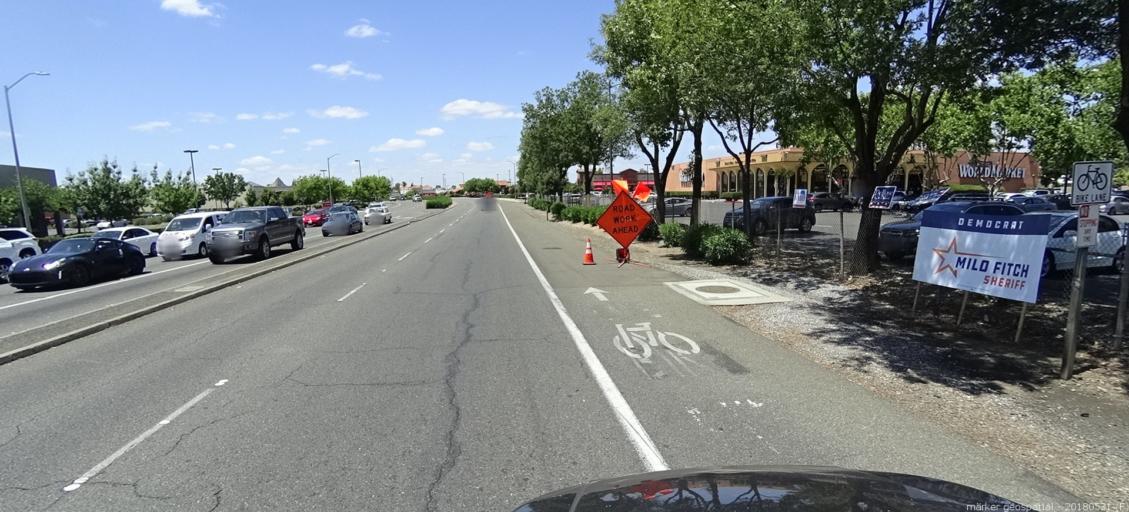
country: US
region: California
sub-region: Sacramento County
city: Arden-Arcade
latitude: 38.5983
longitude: -121.4154
